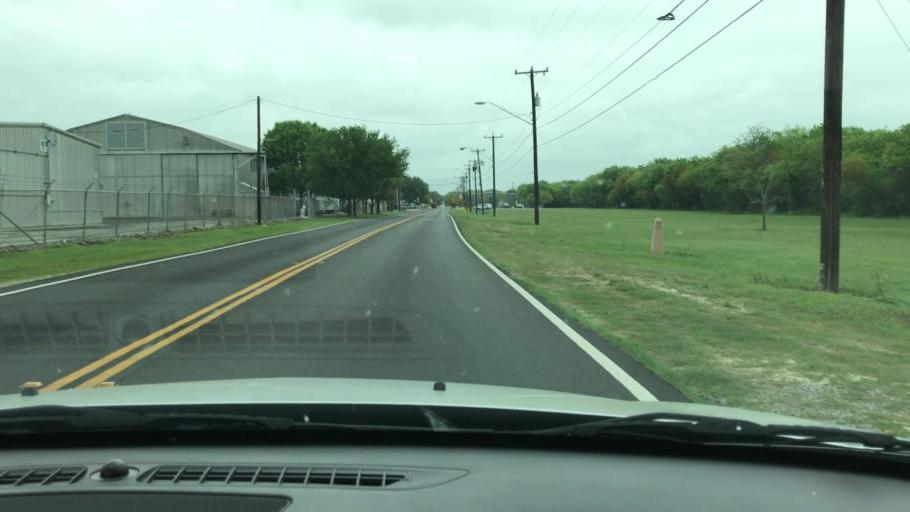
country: US
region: Texas
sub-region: Bexar County
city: San Antonio
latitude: 29.3375
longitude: -98.4659
